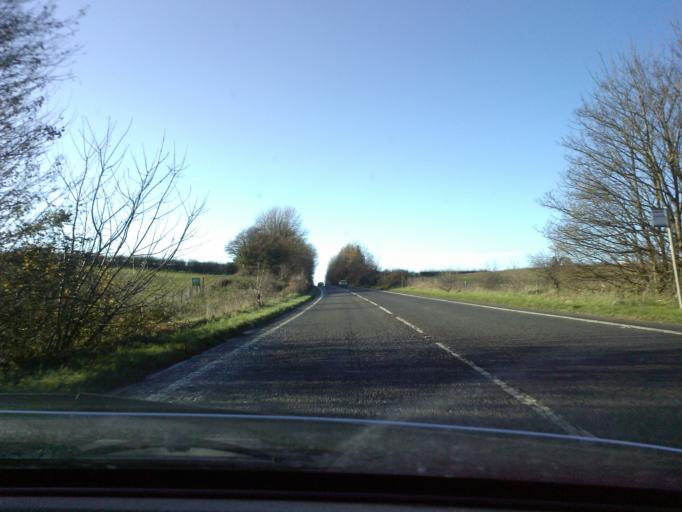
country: GB
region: England
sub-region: Dorset
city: Bridport
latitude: 50.7330
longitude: -2.7051
